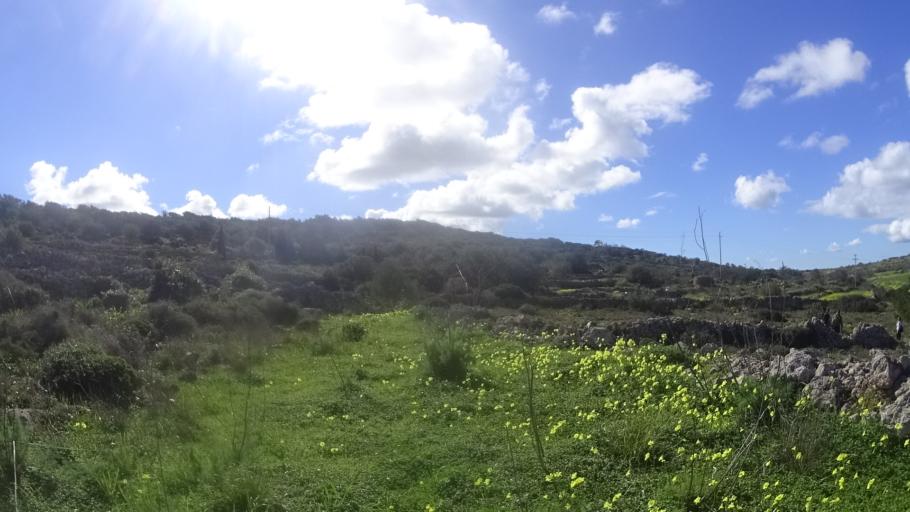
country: MT
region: Il-Mellieha
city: Mellieha
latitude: 35.9504
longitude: 14.3765
